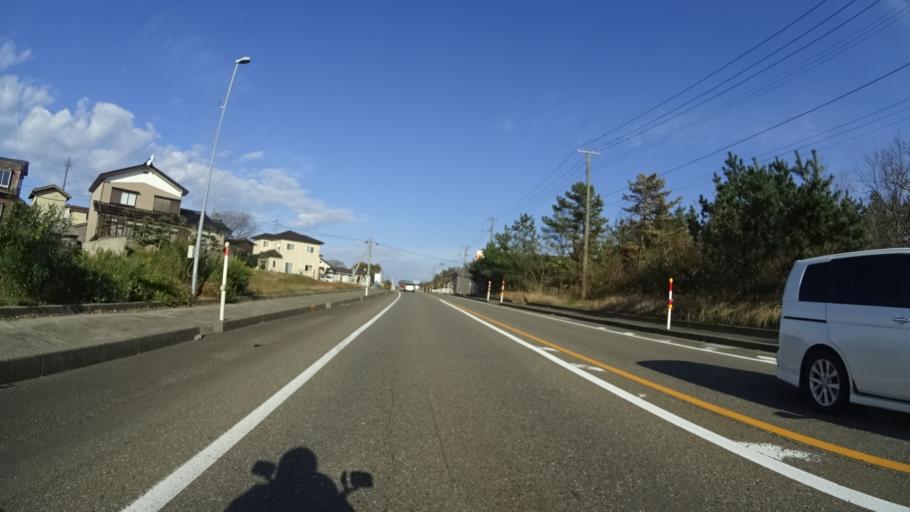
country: JP
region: Niigata
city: Joetsu
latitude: 37.2498
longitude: 138.3570
